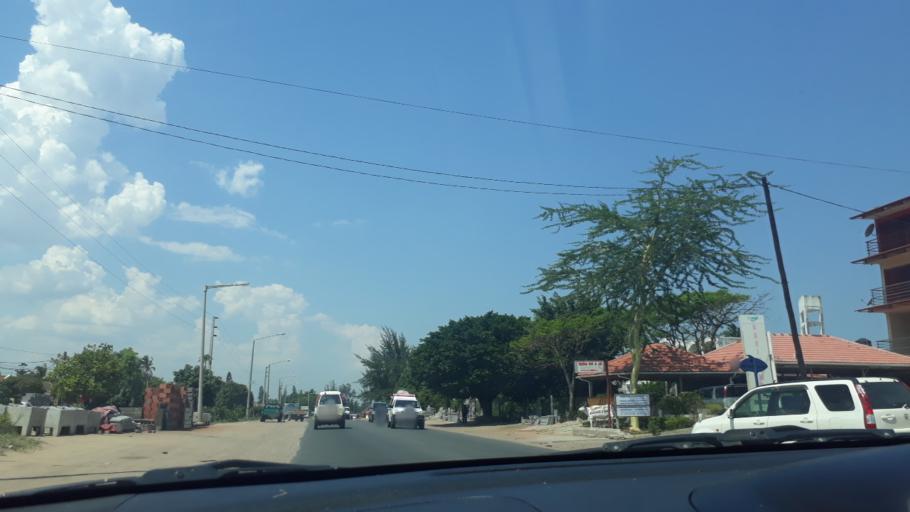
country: MZ
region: Maputo
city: Matola
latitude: -25.9599
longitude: 32.4503
